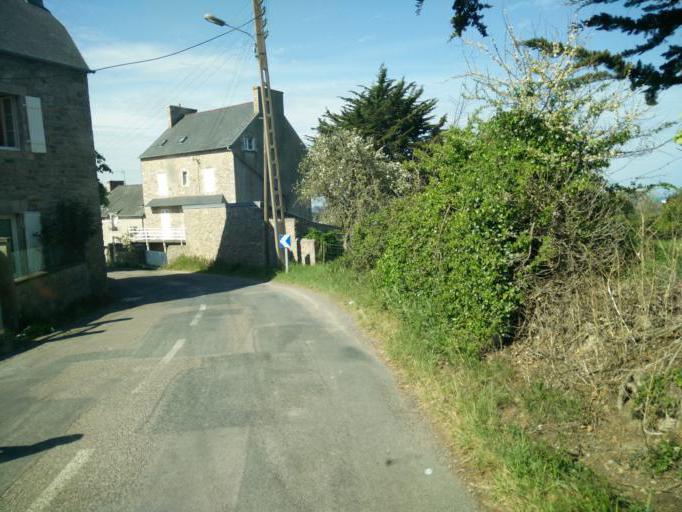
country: FR
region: Brittany
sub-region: Departement des Cotes-d'Armor
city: Erquy
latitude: 48.6354
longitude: -2.4597
